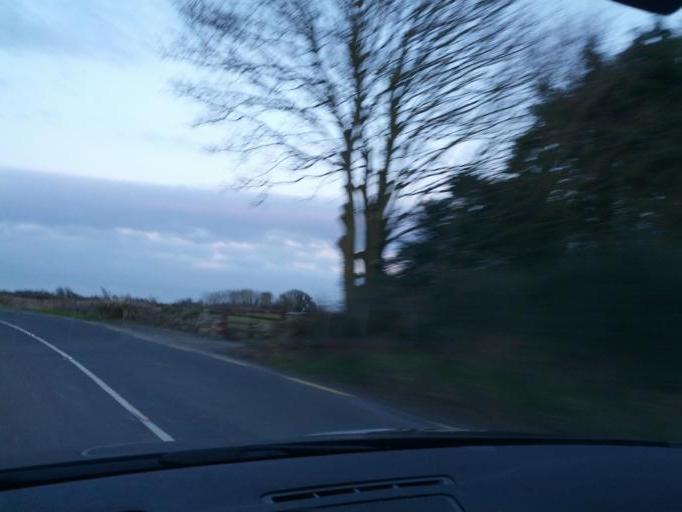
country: IE
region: Leinster
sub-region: Uibh Fhaili
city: Banagher
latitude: 53.0949
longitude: -8.0307
